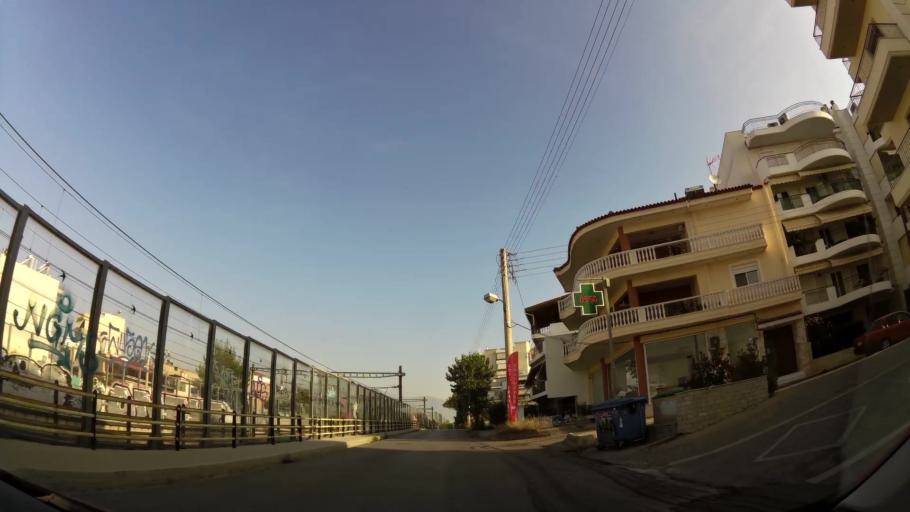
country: GR
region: Attica
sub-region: Nomarchia Athinas
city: Nea Filadelfeia
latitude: 38.0489
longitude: 23.7316
